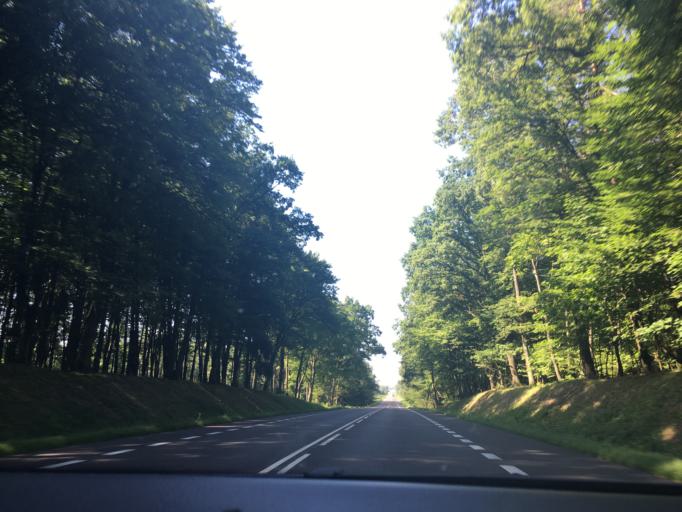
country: PL
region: Lublin Voivodeship
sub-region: Powiat radzynski
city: Borki
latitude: 51.7309
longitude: 22.5413
